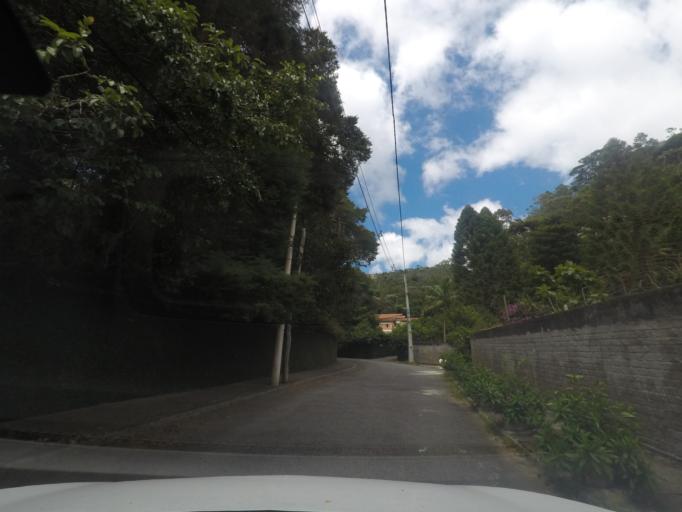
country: BR
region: Rio de Janeiro
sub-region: Teresopolis
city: Teresopolis
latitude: -22.4044
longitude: -42.9810
